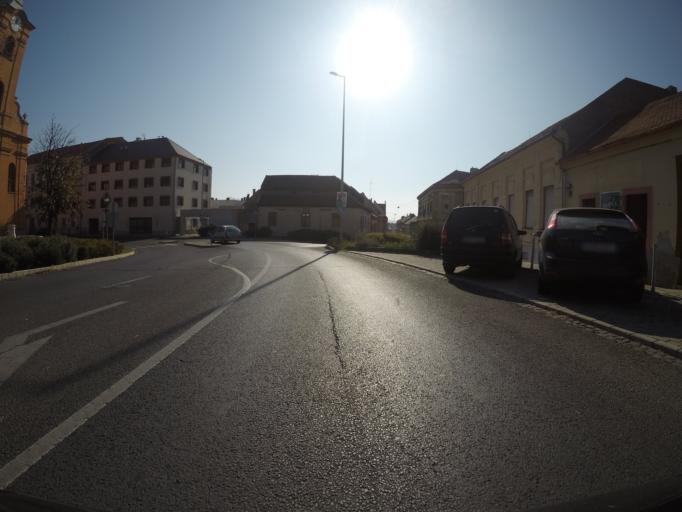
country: HU
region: Baranya
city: Pecs
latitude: 46.0794
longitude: 18.2349
